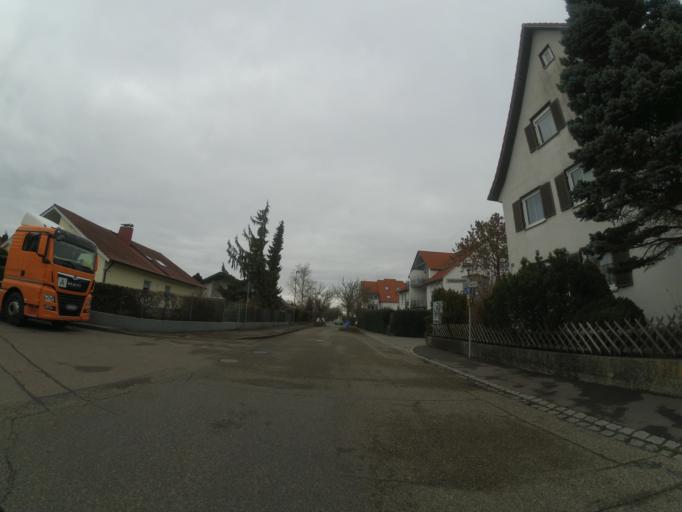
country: DE
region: Bavaria
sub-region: Swabia
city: Senden
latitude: 48.3005
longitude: 10.0549
